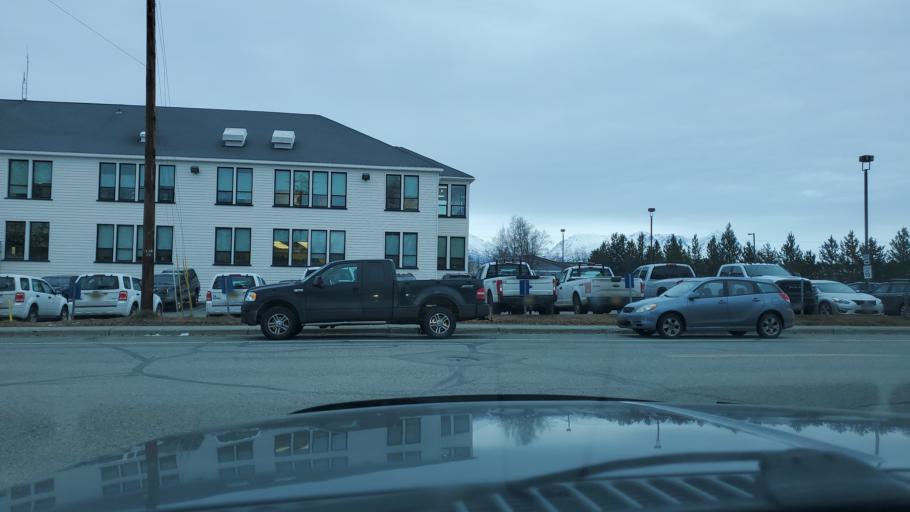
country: US
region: Alaska
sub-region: Matanuska-Susitna Borough
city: Palmer
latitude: 61.5987
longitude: -149.1083
